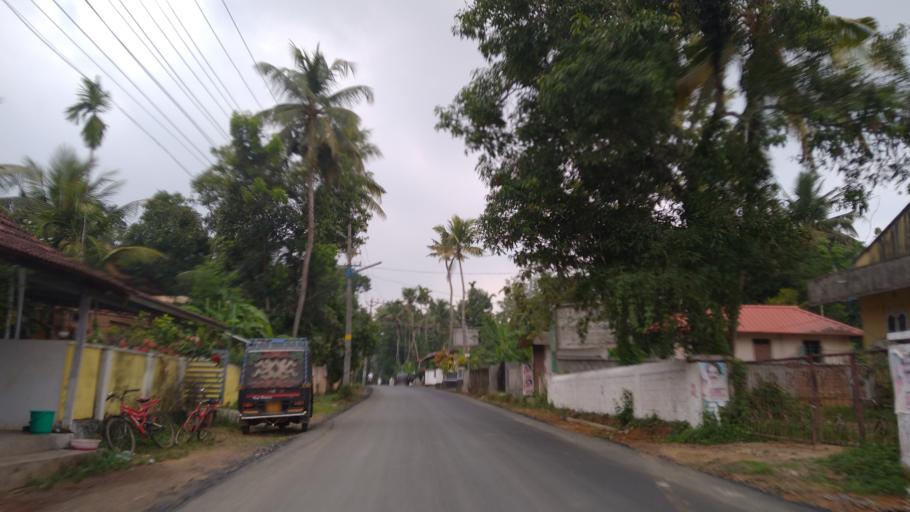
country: IN
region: Kerala
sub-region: Ernakulam
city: Perumbavoor
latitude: 10.0640
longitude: 76.5041
